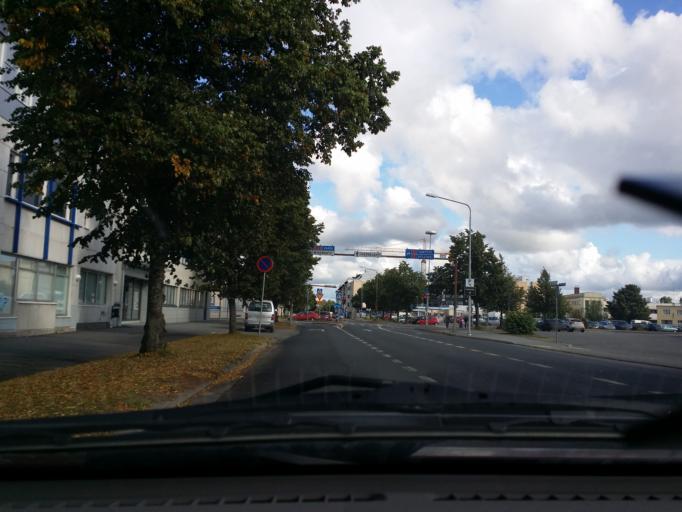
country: FI
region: Satakunta
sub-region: Pori
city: Pori
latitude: 61.4817
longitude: 21.7981
